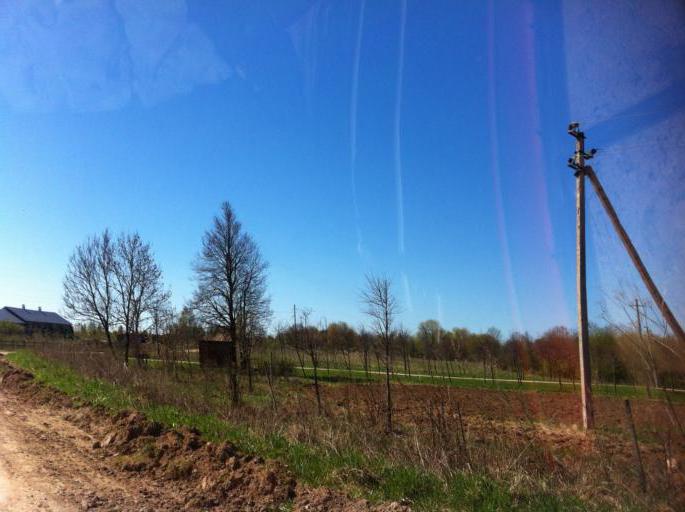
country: RU
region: Pskov
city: Izborsk
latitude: 57.8096
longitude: 27.9798
